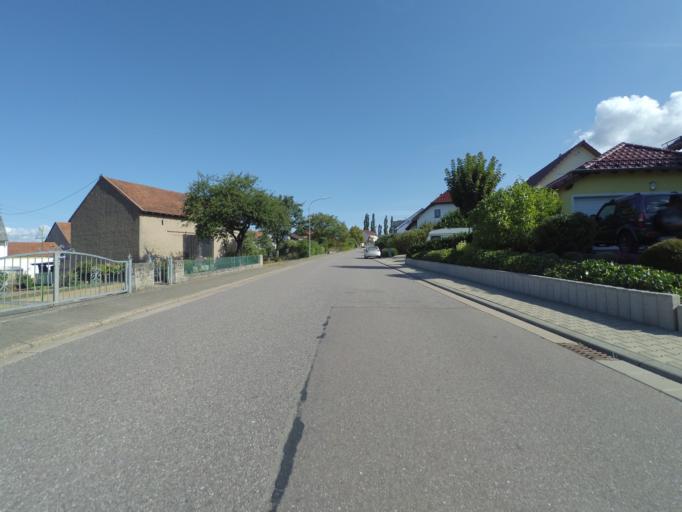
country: LU
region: Grevenmacher
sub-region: Canton de Remich
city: Remich
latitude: 49.5184
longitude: 6.4200
